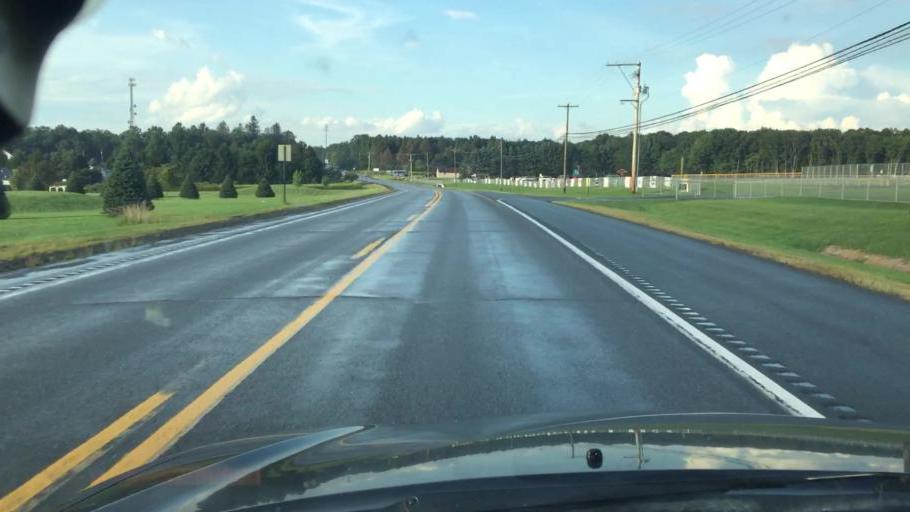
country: US
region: Pennsylvania
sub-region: Carbon County
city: Jim Thorpe
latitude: 40.9310
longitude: -75.6595
